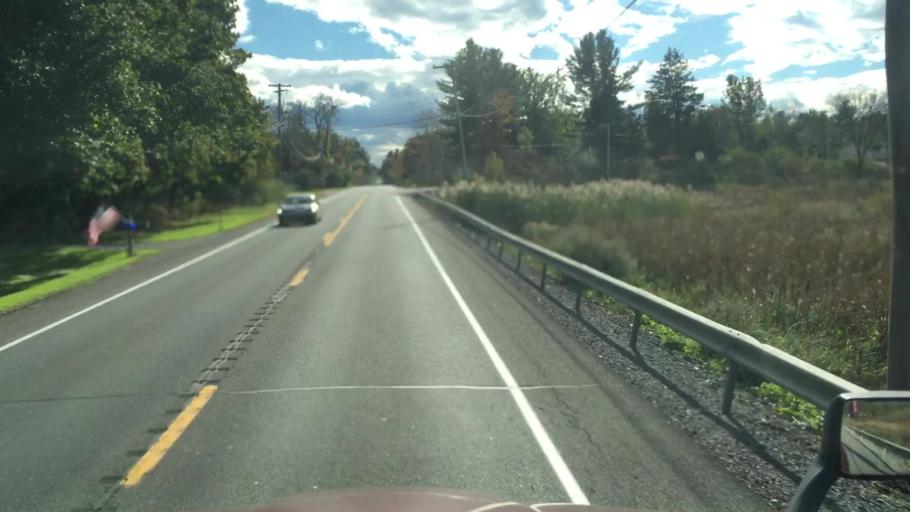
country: US
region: New York
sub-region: Saratoga County
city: Ballston Spa
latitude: 42.9494
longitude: -73.8675
